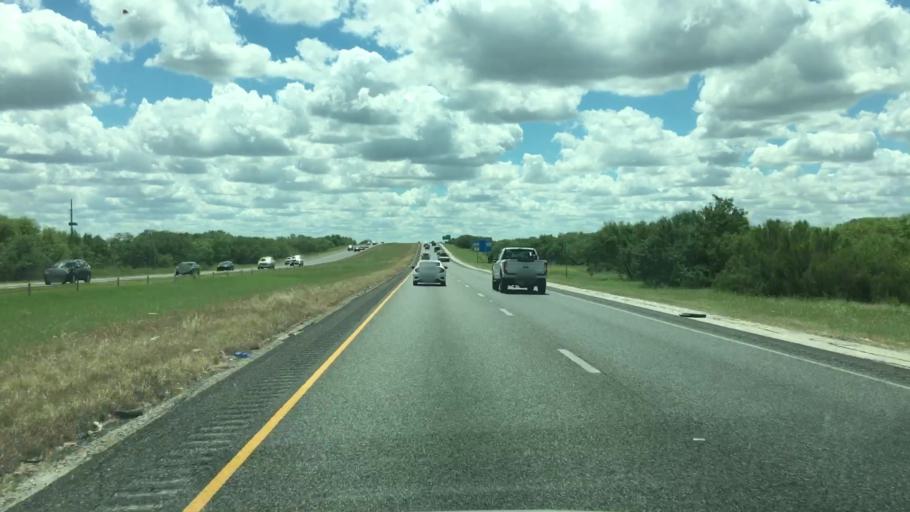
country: US
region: Texas
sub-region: Bexar County
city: Elmendorf
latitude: 29.2956
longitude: -98.3952
